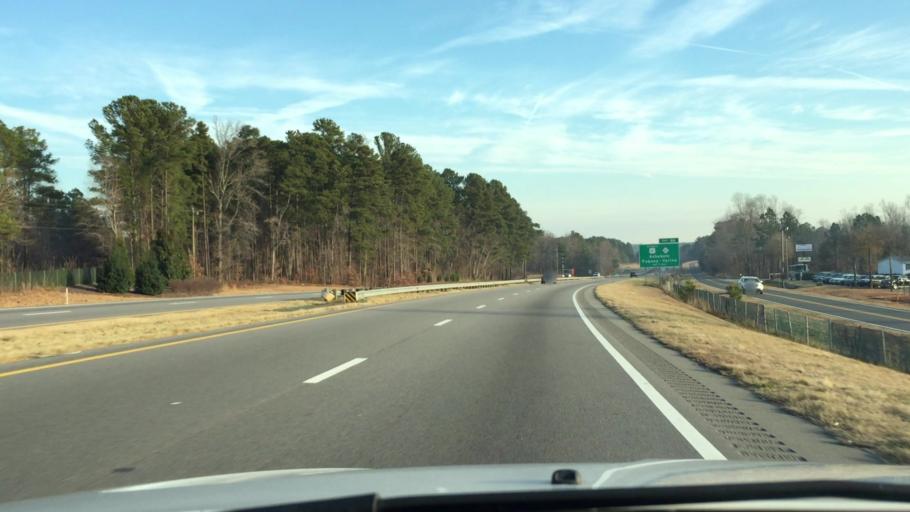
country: US
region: North Carolina
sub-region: Lee County
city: Sanford
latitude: 35.4520
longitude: -79.2137
